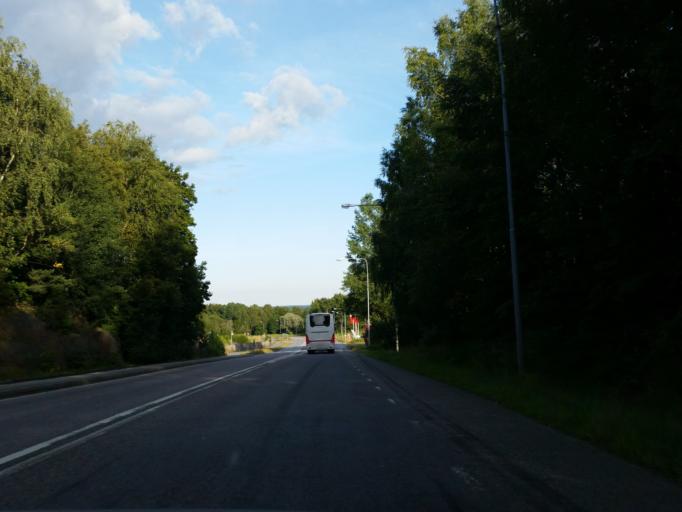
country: SE
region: Stockholm
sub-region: Sodertalje Kommun
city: Pershagen
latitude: 59.0884
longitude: 17.5750
